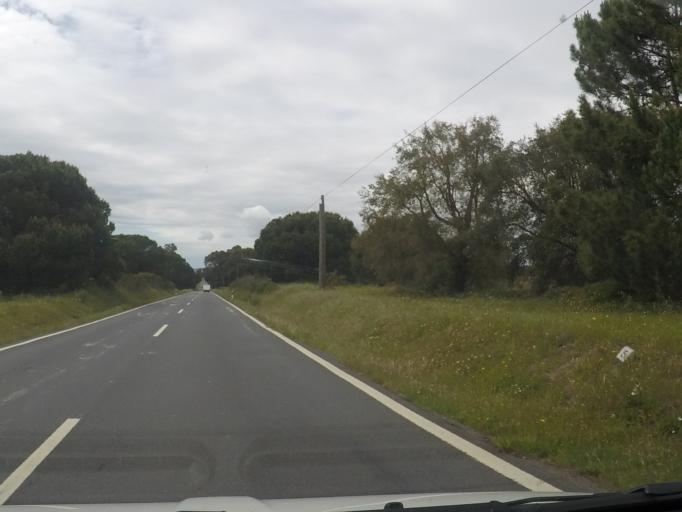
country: PT
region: Setubal
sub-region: Sines
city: Porto Covo
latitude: 37.8808
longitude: -8.7465
